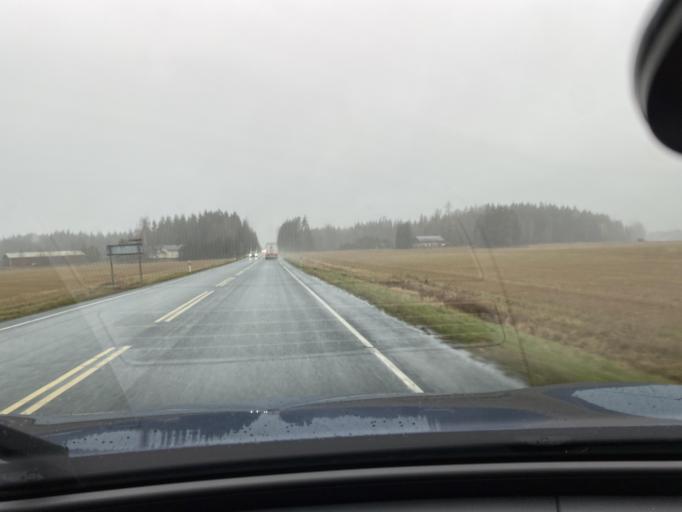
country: FI
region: Haeme
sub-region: Forssa
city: Jokioinen
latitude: 60.7877
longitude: 23.4824
